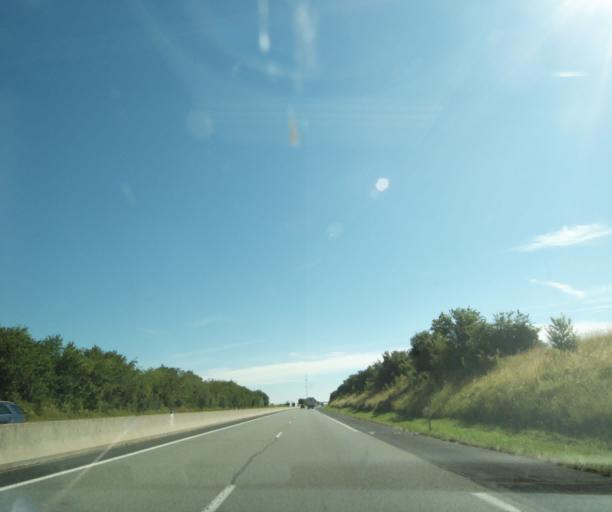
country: FR
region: Lorraine
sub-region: Departement des Vosges
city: Lamarche
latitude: 48.1717
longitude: 5.7208
